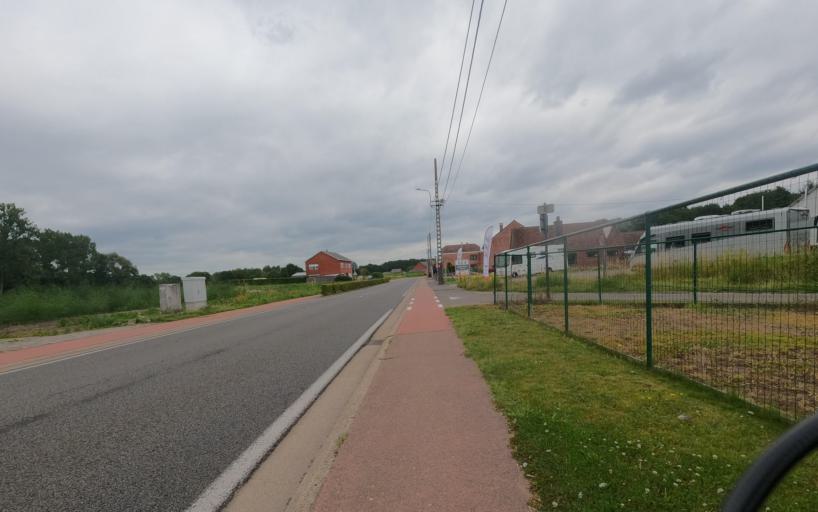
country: BE
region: Flanders
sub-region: Provincie Vlaams-Brabant
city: Tremelo
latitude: 50.9765
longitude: 4.7279
